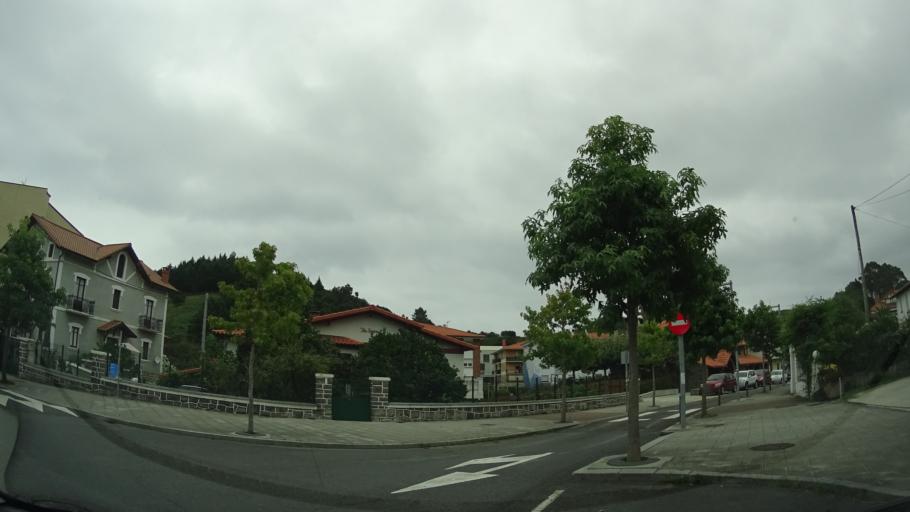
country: ES
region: Basque Country
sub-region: Bizkaia
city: Elexalde
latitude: 43.4319
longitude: -2.8970
